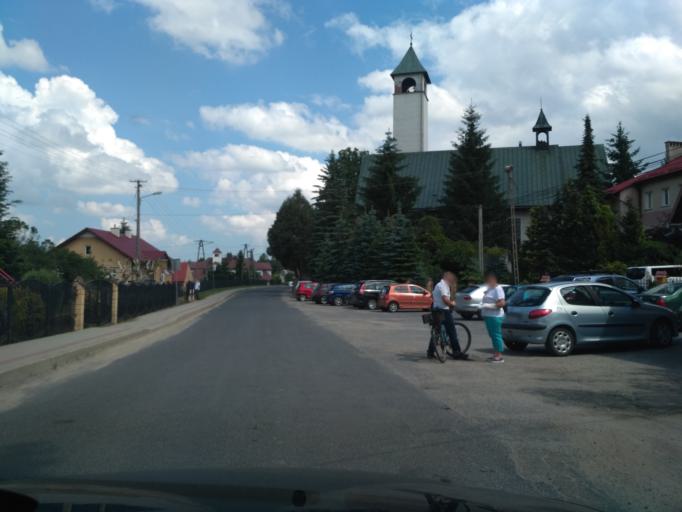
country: PL
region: Subcarpathian Voivodeship
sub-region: Powiat rzeszowski
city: Blazowa
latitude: 49.8585
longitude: 22.0685
